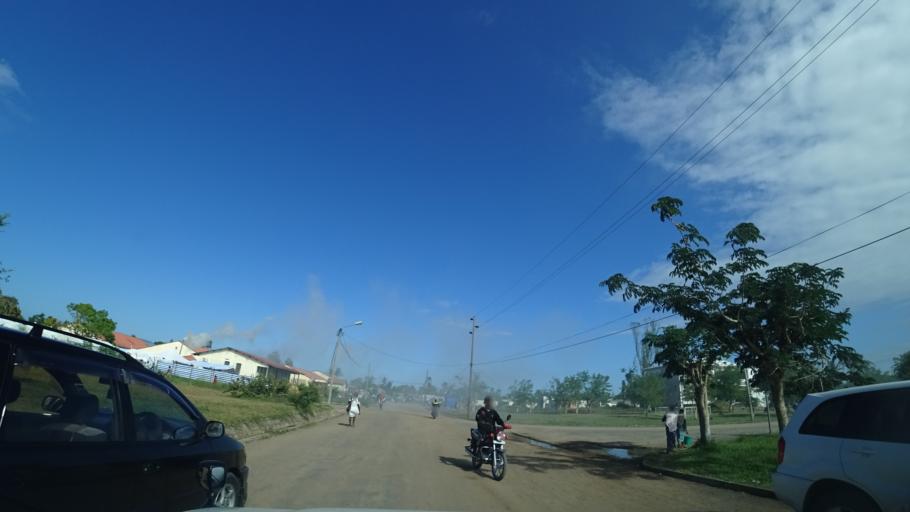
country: MZ
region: Sofala
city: Dondo
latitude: -19.6177
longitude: 34.7421
